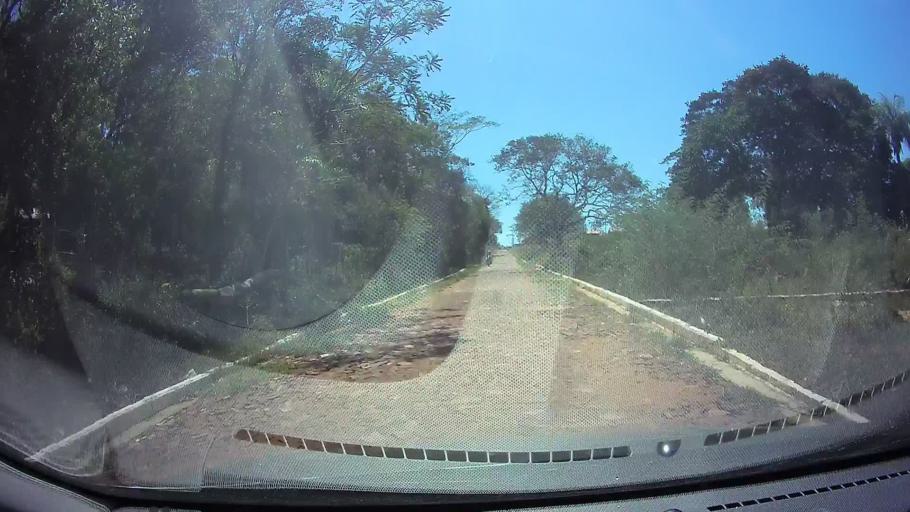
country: PY
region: Central
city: Limpio
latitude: -25.2318
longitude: -57.4373
